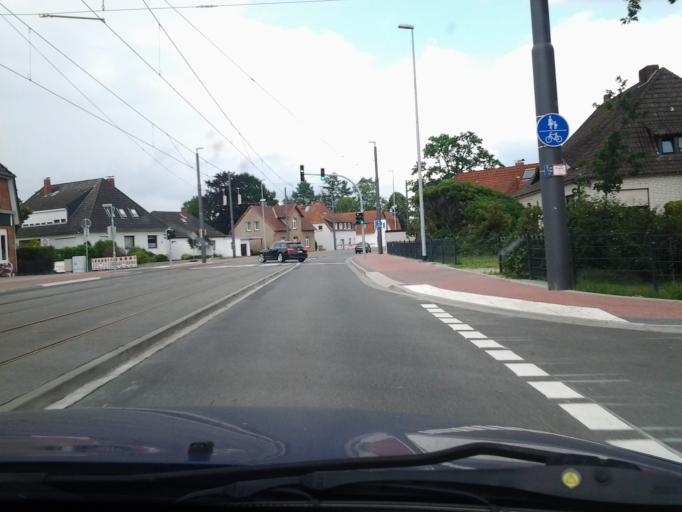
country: DE
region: Lower Saxony
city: Lilienthal
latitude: 53.1511
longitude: 8.9177
